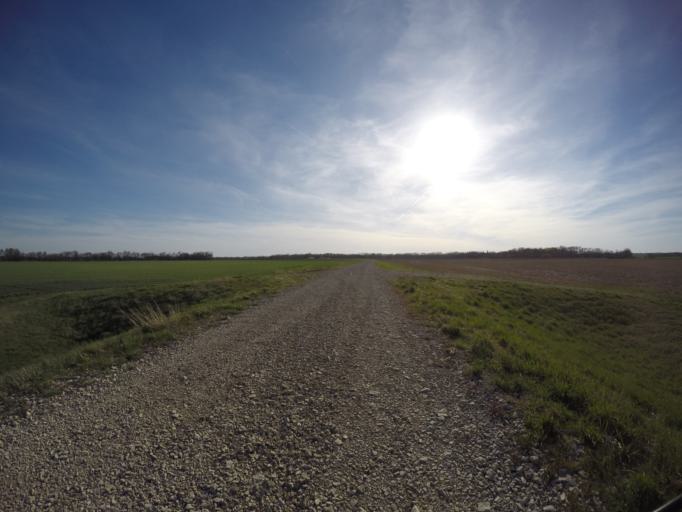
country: US
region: Kansas
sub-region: Saline County
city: Salina
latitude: 38.8602
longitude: -97.6265
